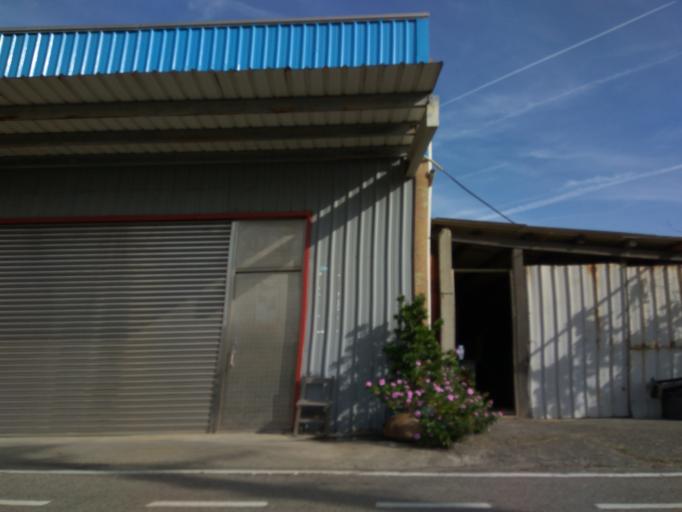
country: TW
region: Taiwan
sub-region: Hsinchu
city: Zhubei
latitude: 24.9876
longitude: 121.0195
